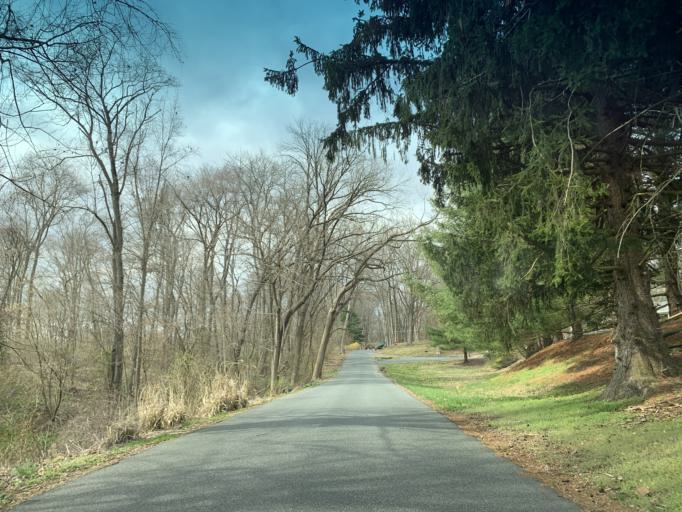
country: US
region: Maryland
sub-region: Harford County
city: North Bel Air
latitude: 39.5171
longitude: -76.3673
